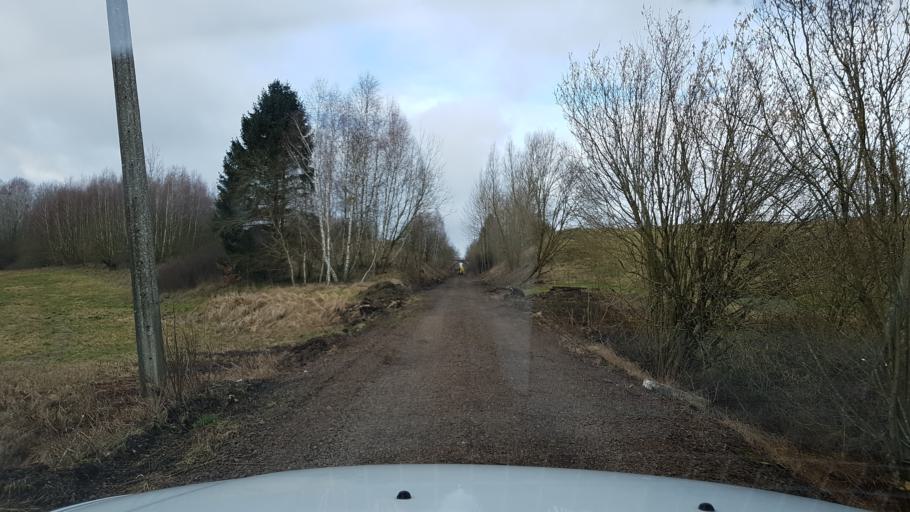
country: PL
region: West Pomeranian Voivodeship
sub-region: Powiat swidwinski
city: Polczyn-Zdroj
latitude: 53.7795
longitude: 16.0733
